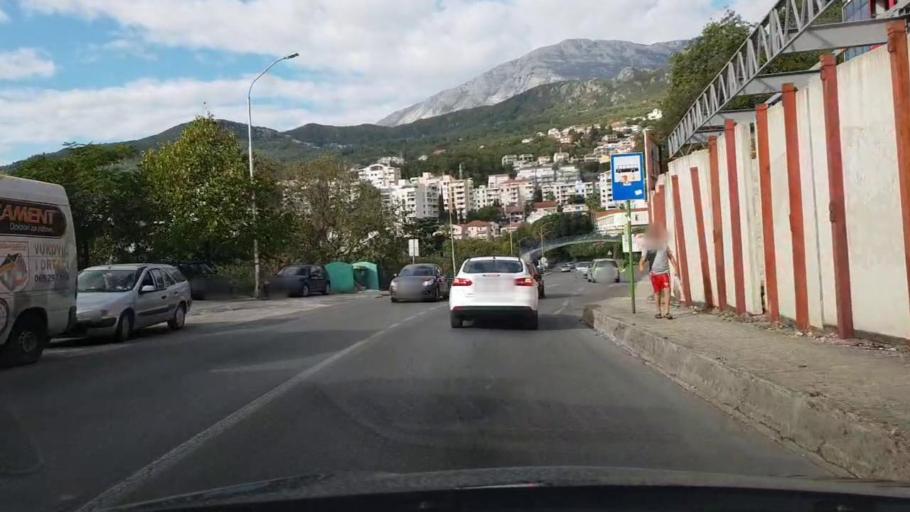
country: ME
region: Herceg Novi
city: Herceg-Novi
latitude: 42.4565
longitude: 18.5271
